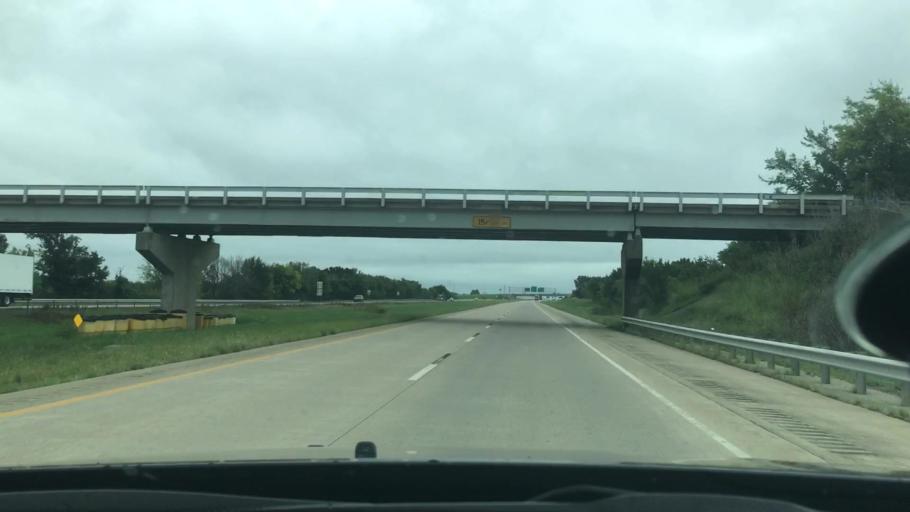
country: US
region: Oklahoma
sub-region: McIntosh County
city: Checotah
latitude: 35.4579
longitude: -95.5577
